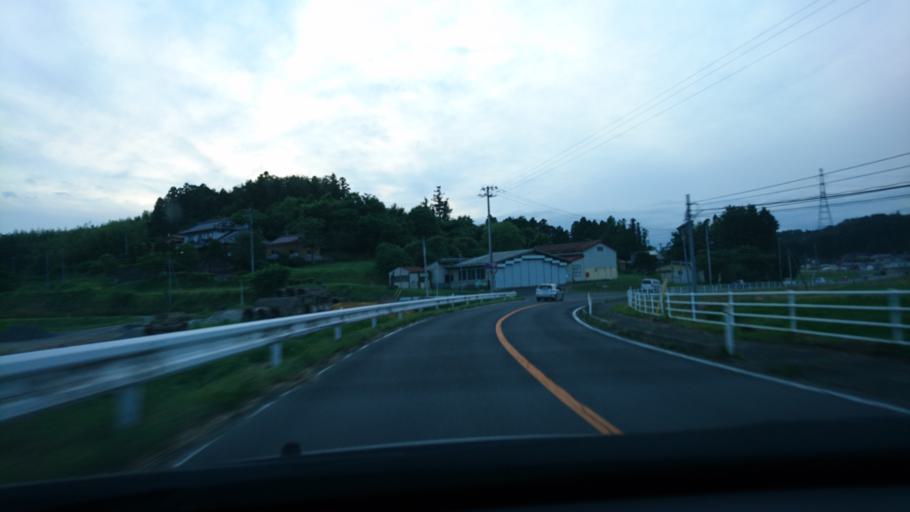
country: JP
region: Iwate
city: Ichinoseki
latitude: 38.7807
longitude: 140.9900
